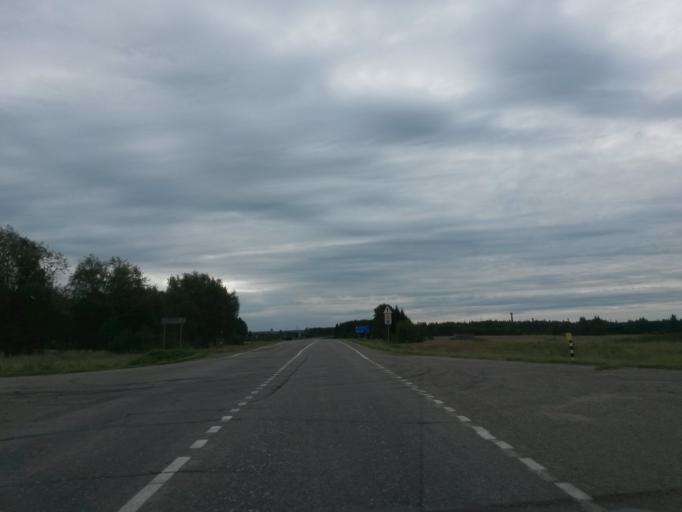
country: RU
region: Jaroslavl
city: Gavrilov-Yam
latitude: 57.3280
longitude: 39.8196
